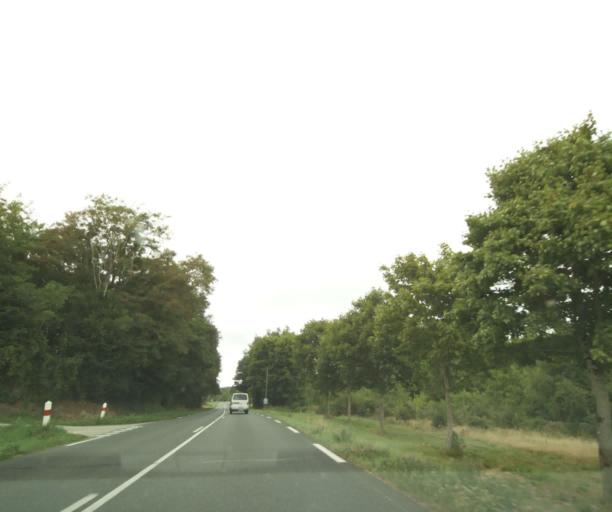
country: FR
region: Centre
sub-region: Departement d'Indre-et-Loire
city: Perrusson
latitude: 47.0662
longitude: 1.0799
